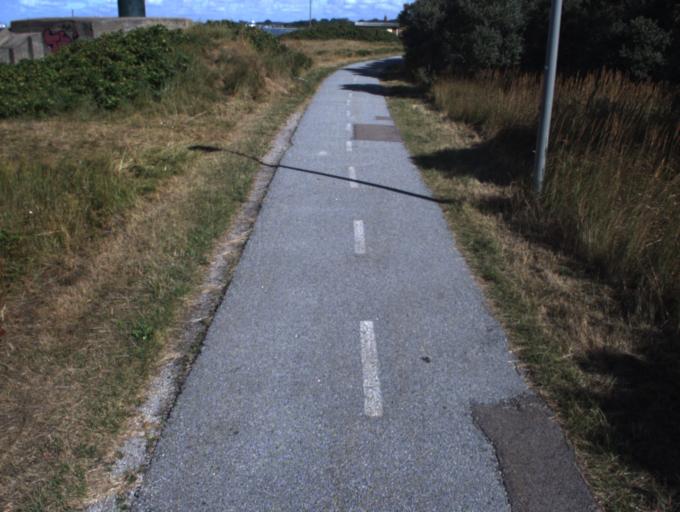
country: SE
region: Skane
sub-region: Helsingborg
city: Rydeback
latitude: 55.9733
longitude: 12.7565
